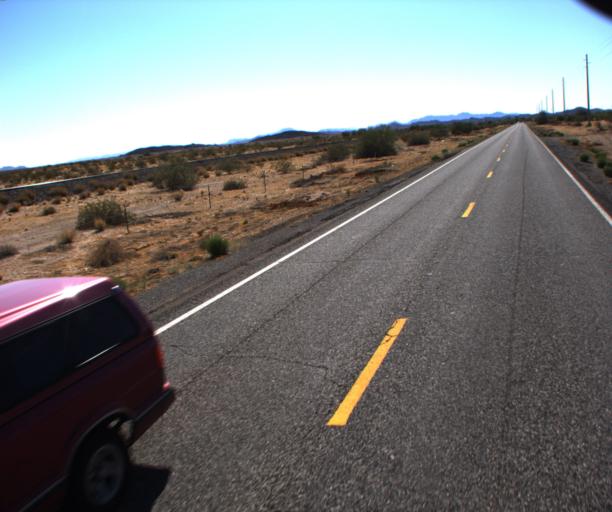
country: US
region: Arizona
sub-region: La Paz County
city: Cienega Springs
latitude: 33.9783
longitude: -114.0543
